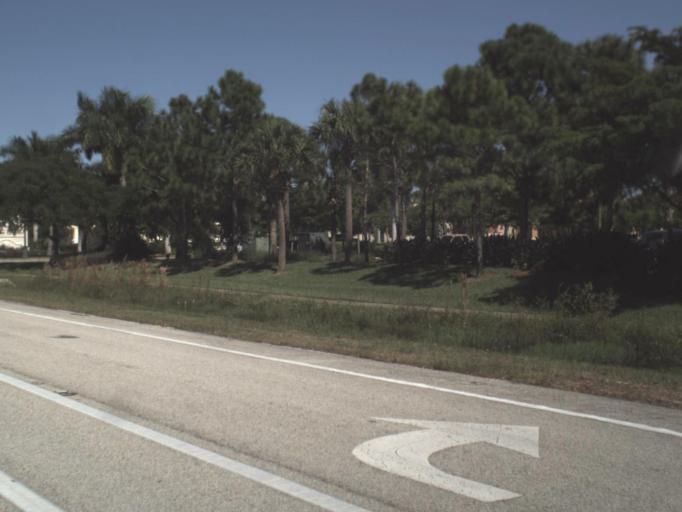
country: US
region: Florida
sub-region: Lee County
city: Estero
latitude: 26.4071
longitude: -81.8112
